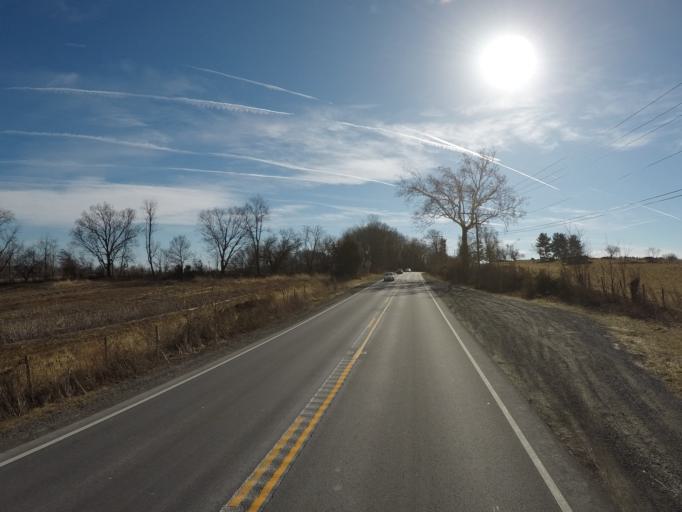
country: US
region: Virginia
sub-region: Loudoun County
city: Leesburg
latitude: 39.1836
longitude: -77.5351
